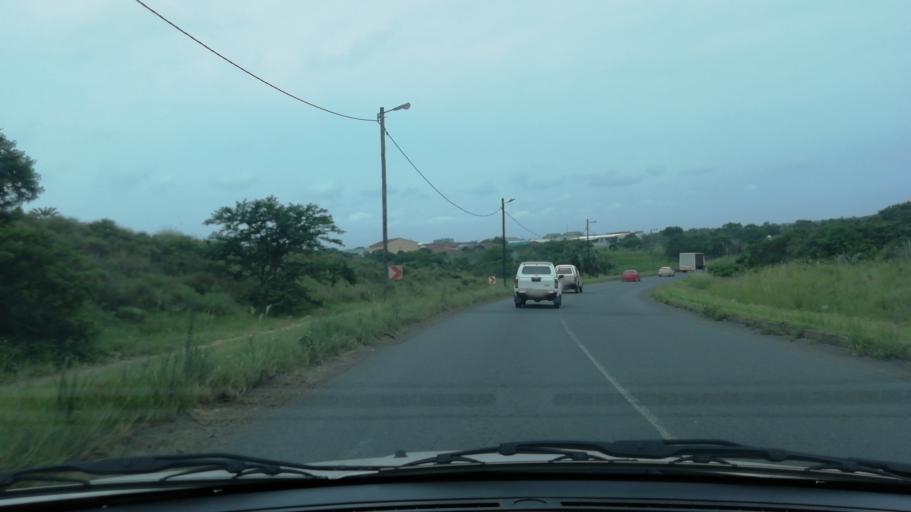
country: ZA
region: KwaZulu-Natal
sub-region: uThungulu District Municipality
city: Richards Bay
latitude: -28.7633
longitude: 32.0385
